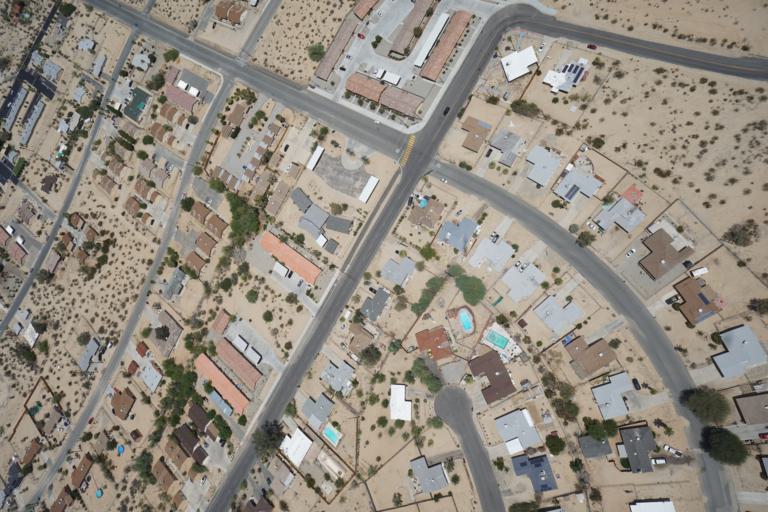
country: US
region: California
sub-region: San Bernardino County
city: Twentynine Palms
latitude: 34.1414
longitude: -116.0580
